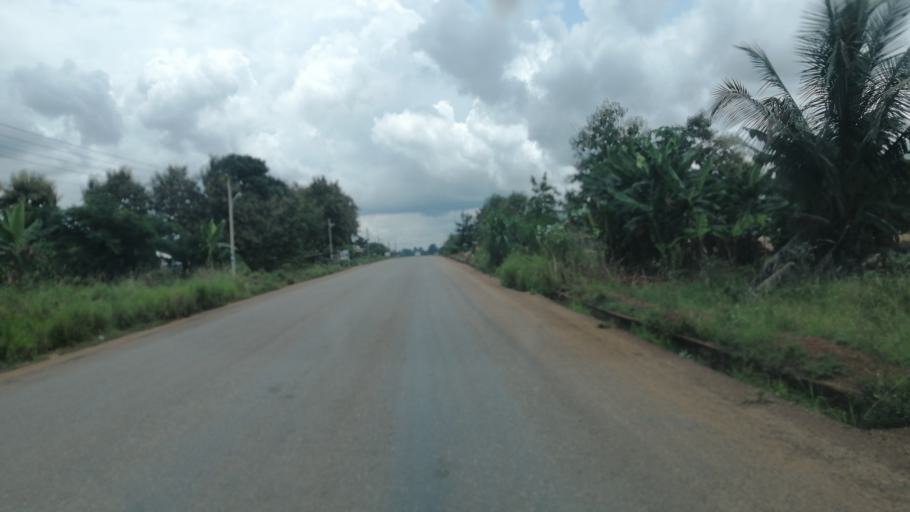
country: GH
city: Duayaw Nkwanta
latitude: 6.9137
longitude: -2.3873
